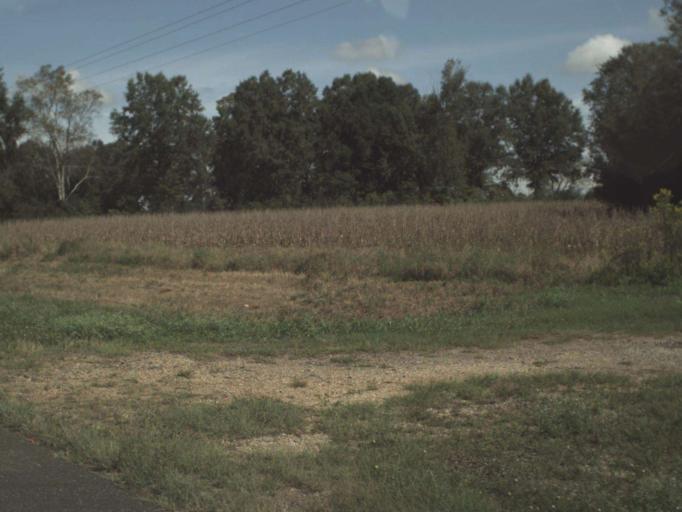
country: US
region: Florida
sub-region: Jackson County
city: Marianna
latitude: 30.8691
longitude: -85.3592
